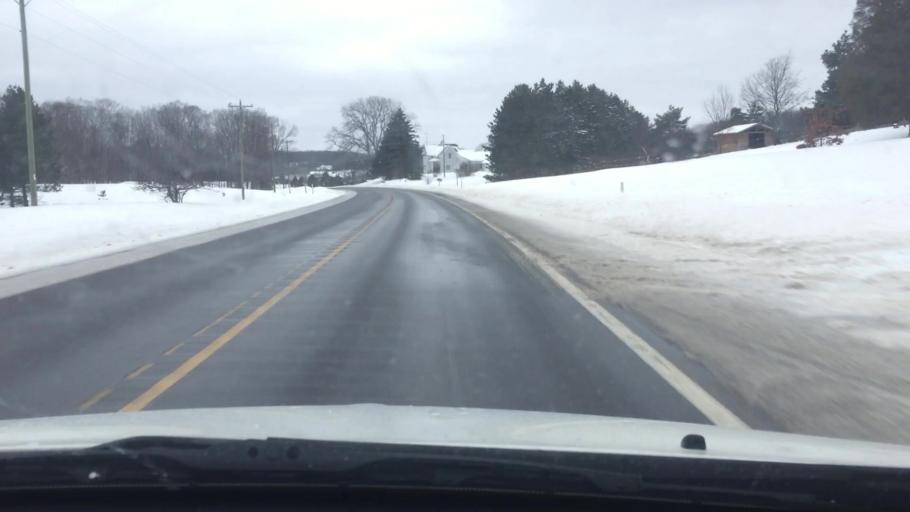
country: US
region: Michigan
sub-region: Charlevoix County
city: Boyne City
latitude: 45.0963
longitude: -84.9832
